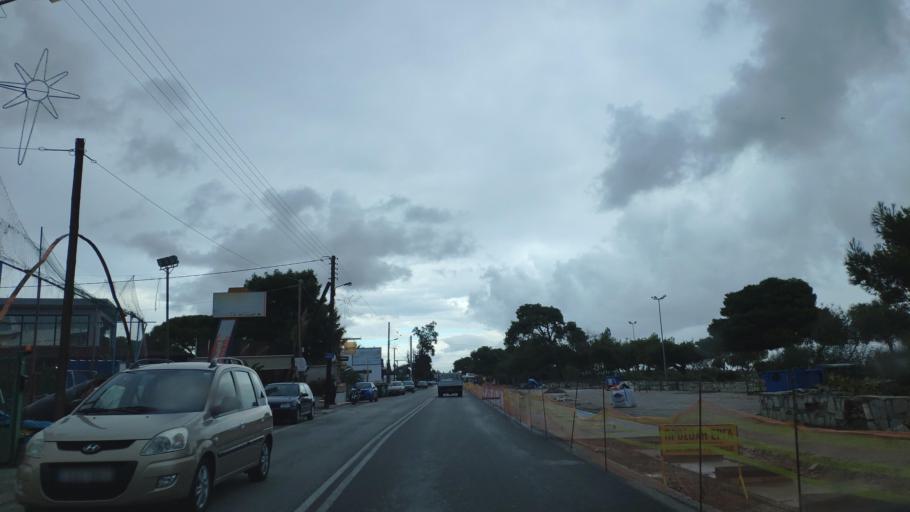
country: GR
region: Attica
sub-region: Nomarchia Anatolikis Attikis
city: Artemida
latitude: 37.9831
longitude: 24.0105
